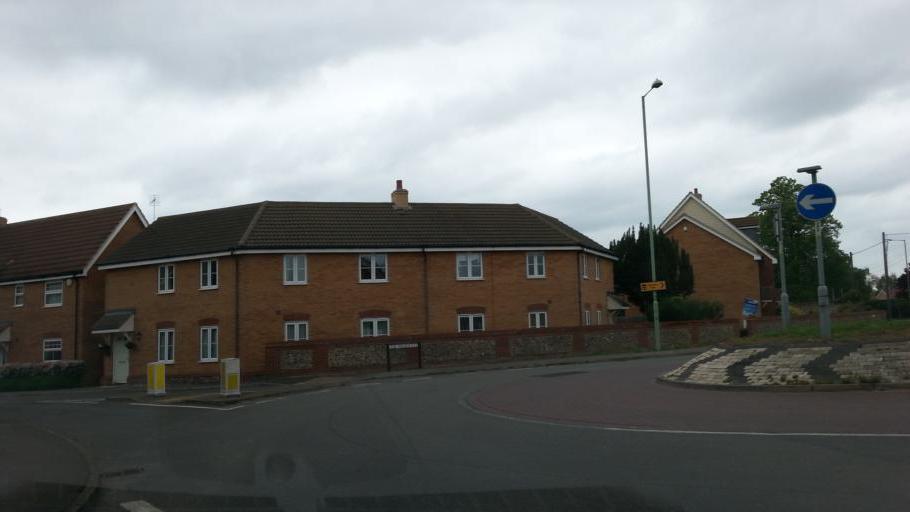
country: GB
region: England
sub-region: Suffolk
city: Lakenheath
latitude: 52.3709
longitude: 0.4844
